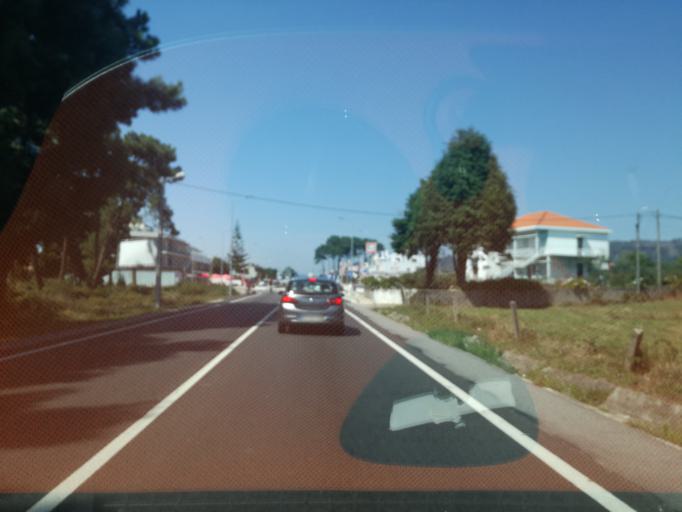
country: PT
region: Braga
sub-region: Esposende
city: Esposende
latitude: 41.5449
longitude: -8.7823
